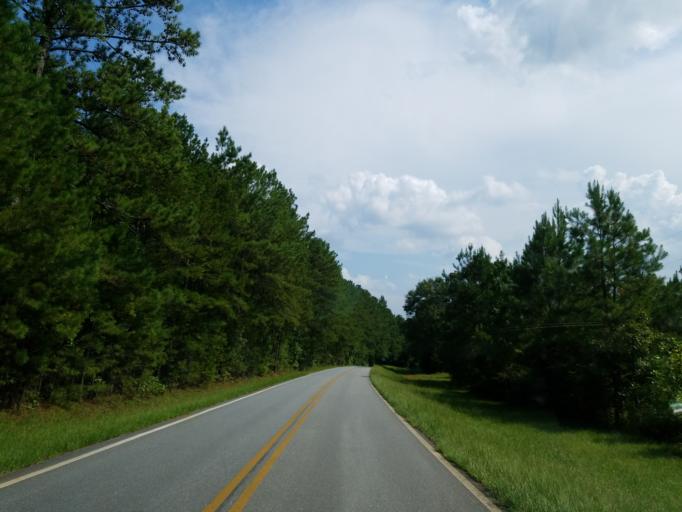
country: US
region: Georgia
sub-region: Monroe County
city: Forsyth
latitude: 33.0045
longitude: -83.8481
